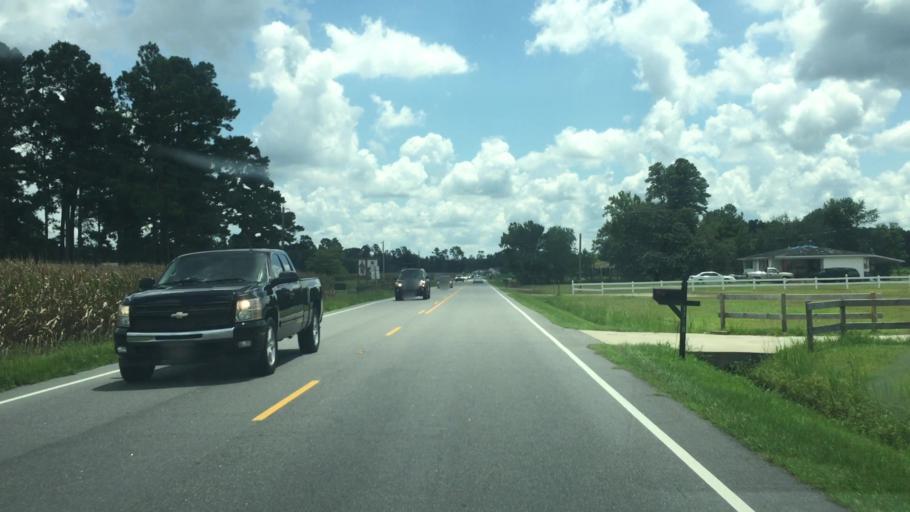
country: US
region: North Carolina
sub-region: Columbus County
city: Chadbourn
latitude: 34.2797
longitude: -78.8164
